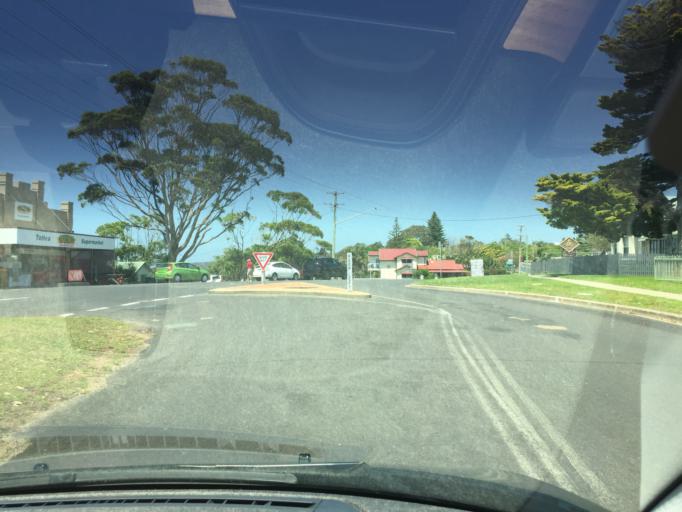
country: AU
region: New South Wales
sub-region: Bega Valley
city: Bega
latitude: -36.7290
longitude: 149.9868
